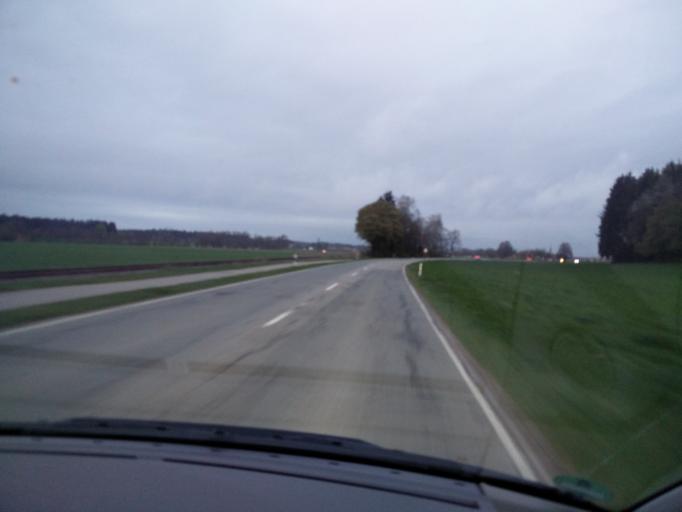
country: DE
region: Bavaria
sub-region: Upper Bavaria
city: Halfing
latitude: 47.9352
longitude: 12.2822
